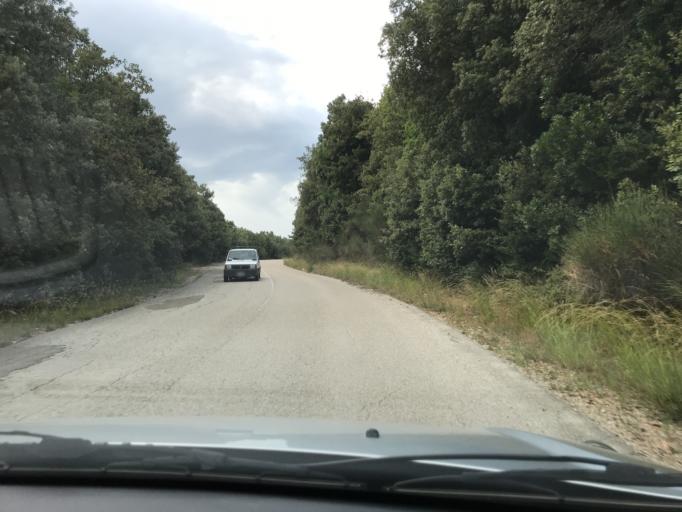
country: IT
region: Umbria
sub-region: Provincia di Terni
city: Montecchio
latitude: 42.6831
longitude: 12.3003
